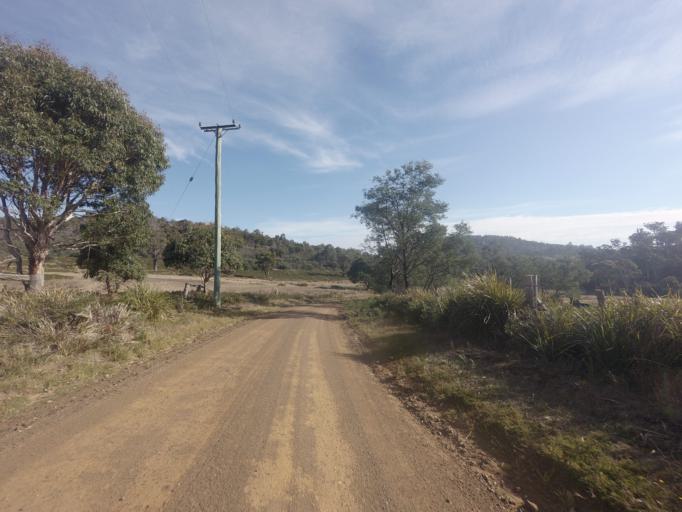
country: AU
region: Tasmania
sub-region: Sorell
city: Sorell
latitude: -42.5308
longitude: 147.4431
